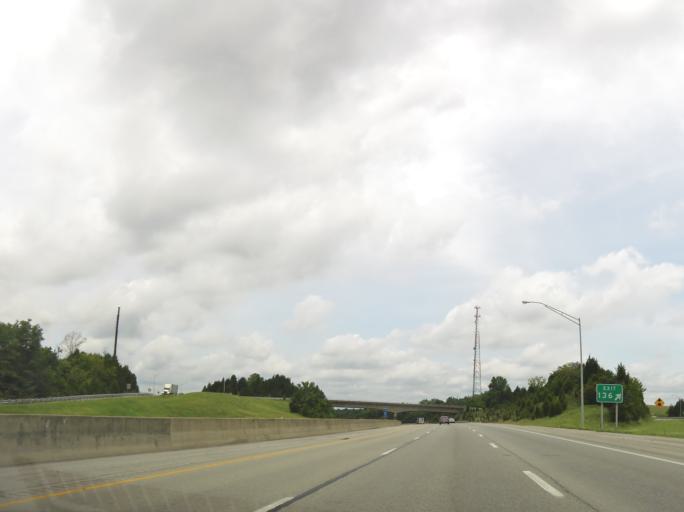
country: US
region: Kentucky
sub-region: Scott County
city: Georgetown
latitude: 38.3773
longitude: -84.5702
